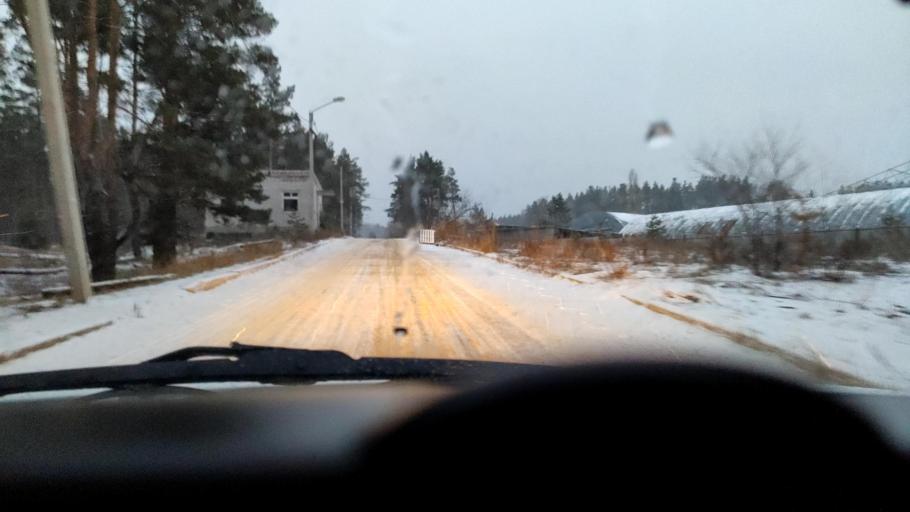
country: RU
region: Voronezj
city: Pridonskoy
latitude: 51.7034
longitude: 39.1057
